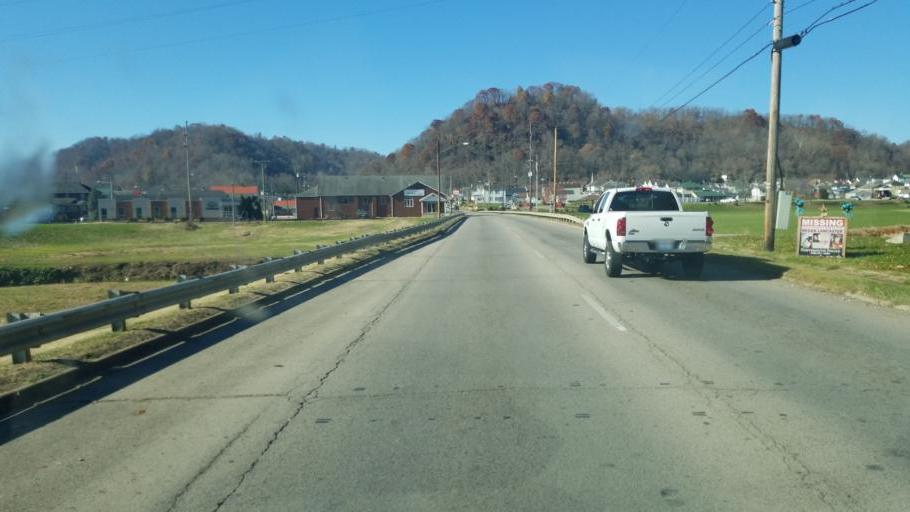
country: US
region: Ohio
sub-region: Scioto County
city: New Boston
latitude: 38.7548
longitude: -82.9266
